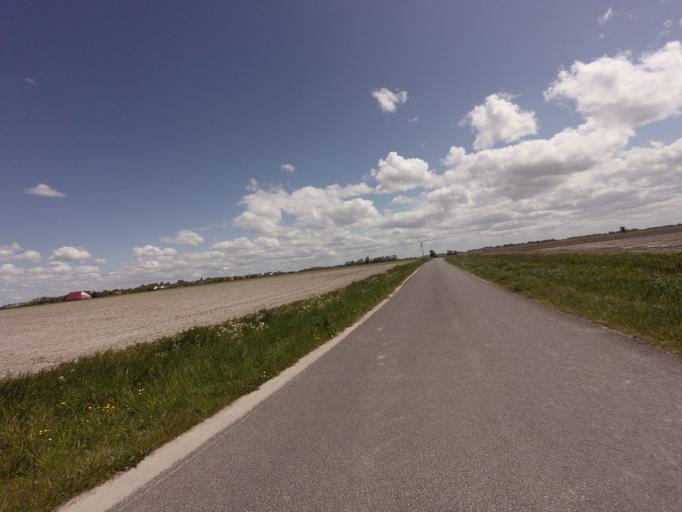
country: NL
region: Friesland
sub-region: Gemeente Harlingen
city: Harlingen
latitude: 53.1392
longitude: 5.4227
